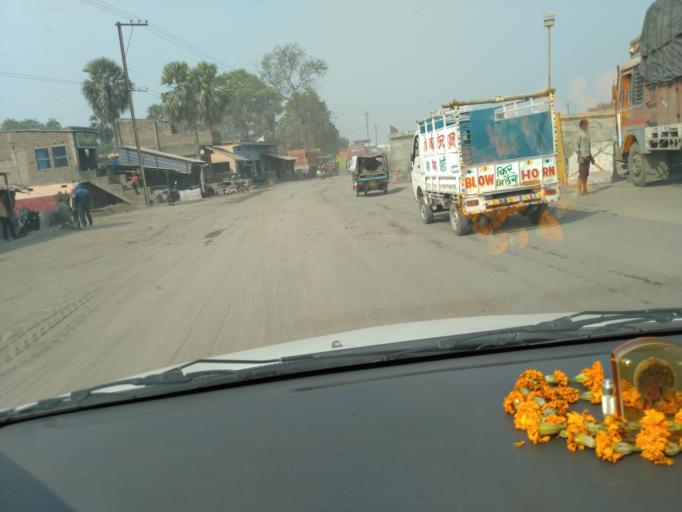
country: IN
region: Bihar
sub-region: Rohtas
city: Dehri
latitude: 24.9148
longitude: 84.1594
